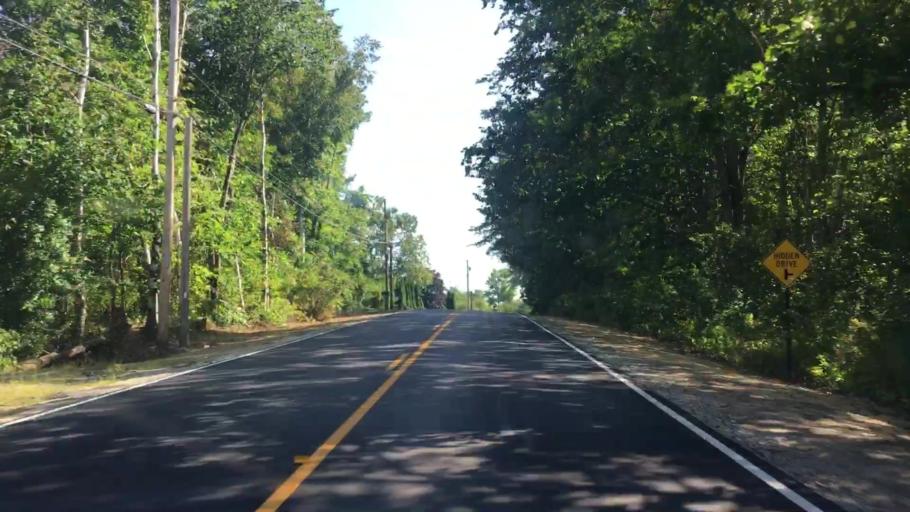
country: US
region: Maine
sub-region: Androscoggin County
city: Sabattus
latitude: 44.1247
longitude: -70.0857
